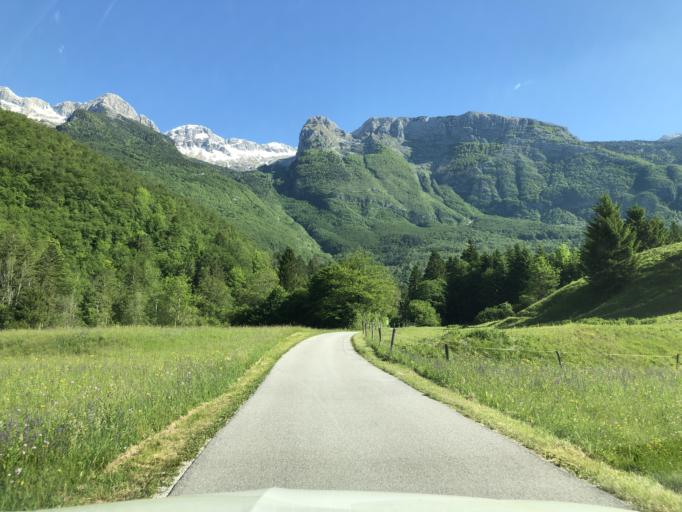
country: SI
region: Bovec
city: Bovec
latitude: 46.3259
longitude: 13.5177
